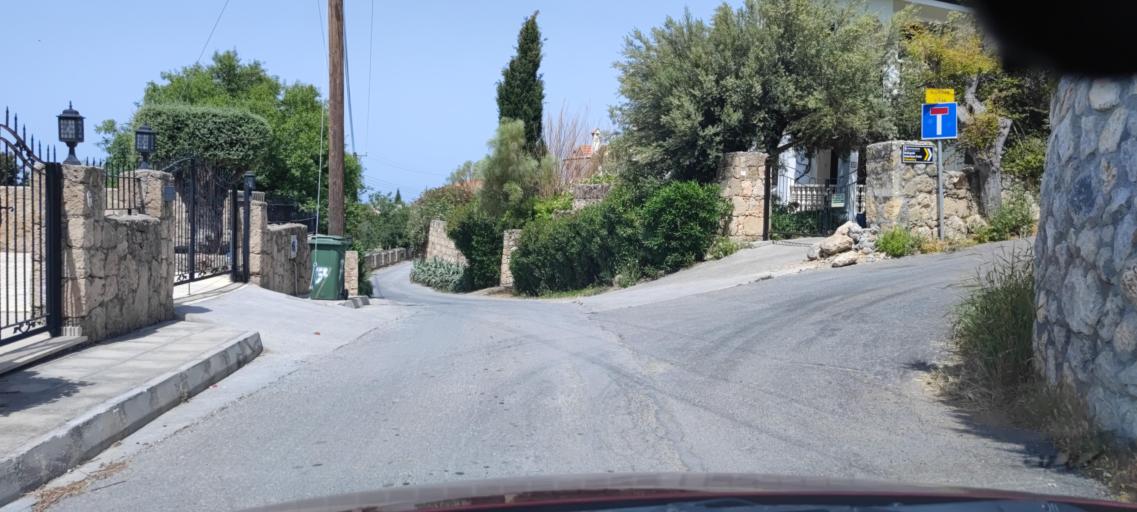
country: CY
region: Keryneia
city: Kyrenia
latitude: 35.3098
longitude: 33.3569
